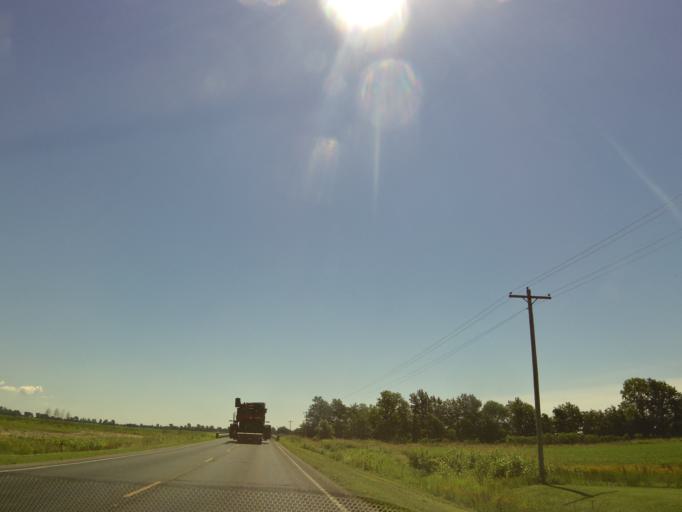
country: US
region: Missouri
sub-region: New Madrid County
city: Portageville
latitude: 36.5538
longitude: -89.7569
